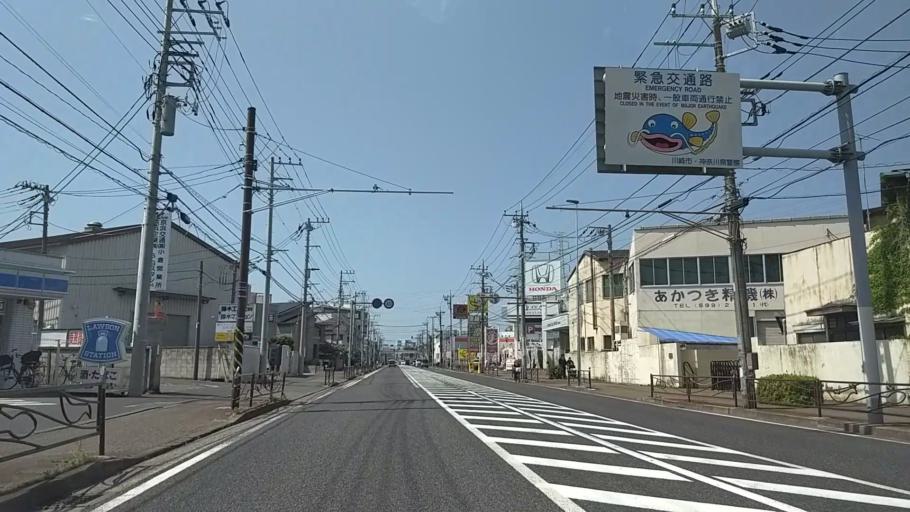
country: JP
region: Kanagawa
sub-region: Kawasaki-shi
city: Kawasaki
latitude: 35.5355
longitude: 139.6664
